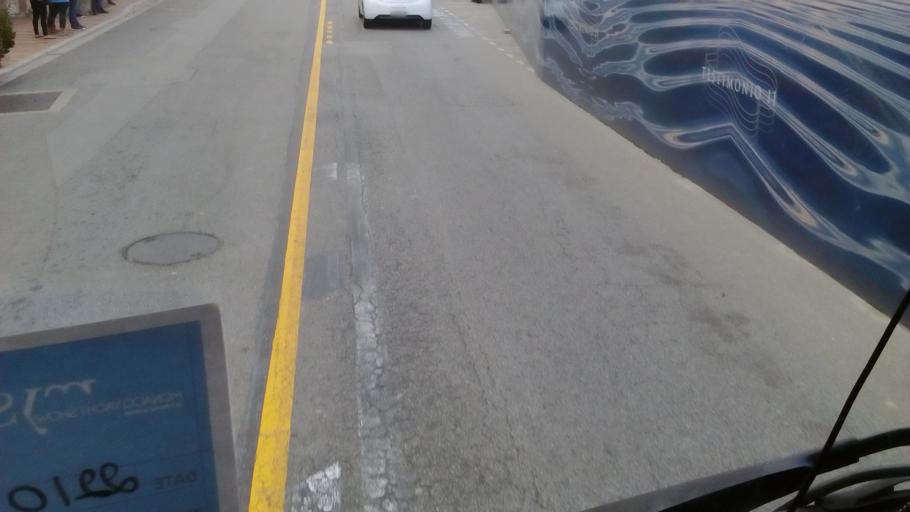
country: MC
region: Commune de Monaco
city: Saint-Roman
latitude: 43.7500
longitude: 7.4371
